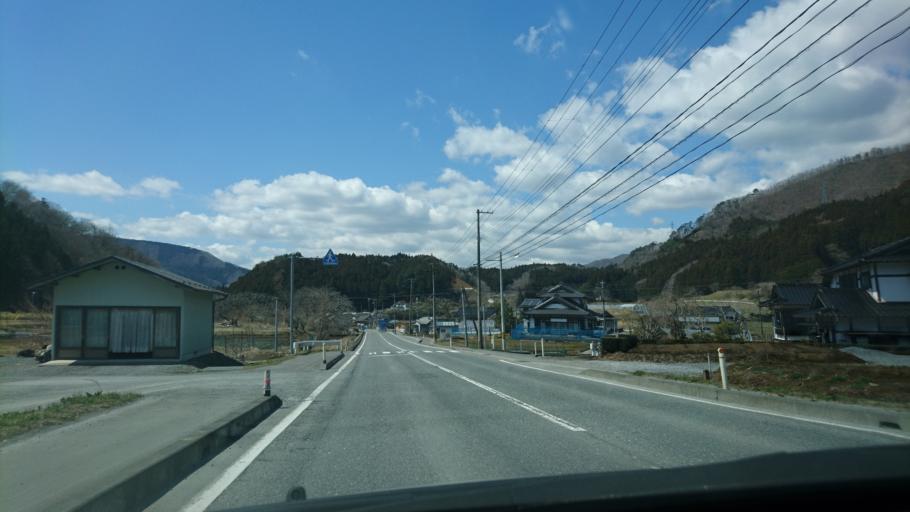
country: JP
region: Iwate
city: Ofunato
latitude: 39.1451
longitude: 141.6014
